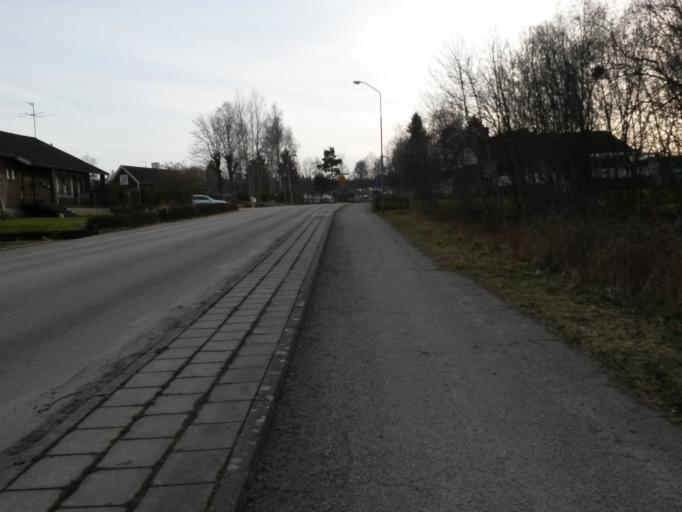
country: SE
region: Vaestra Goetaland
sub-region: Herrljunga Kommun
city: Herrljunga
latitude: 58.0721
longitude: 13.0242
